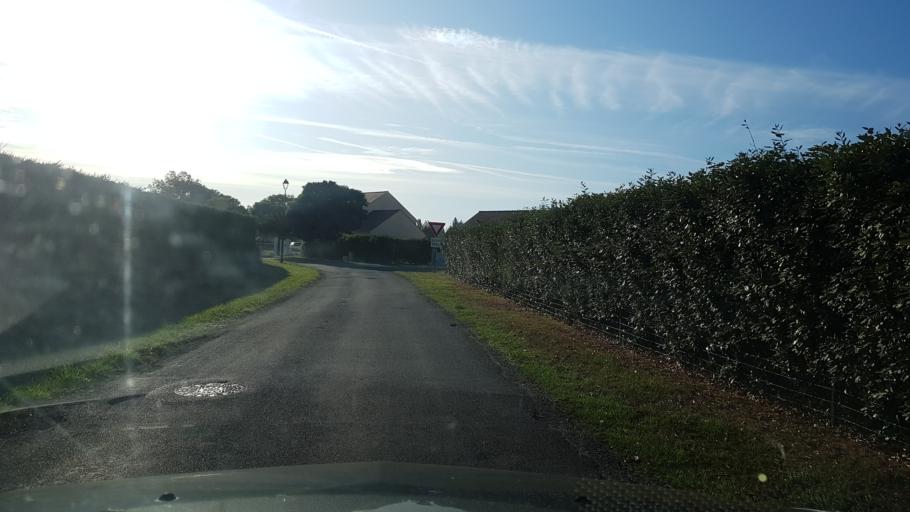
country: FR
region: Centre
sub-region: Departement du Loiret
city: Cerdon
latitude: 47.6879
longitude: 2.3385
